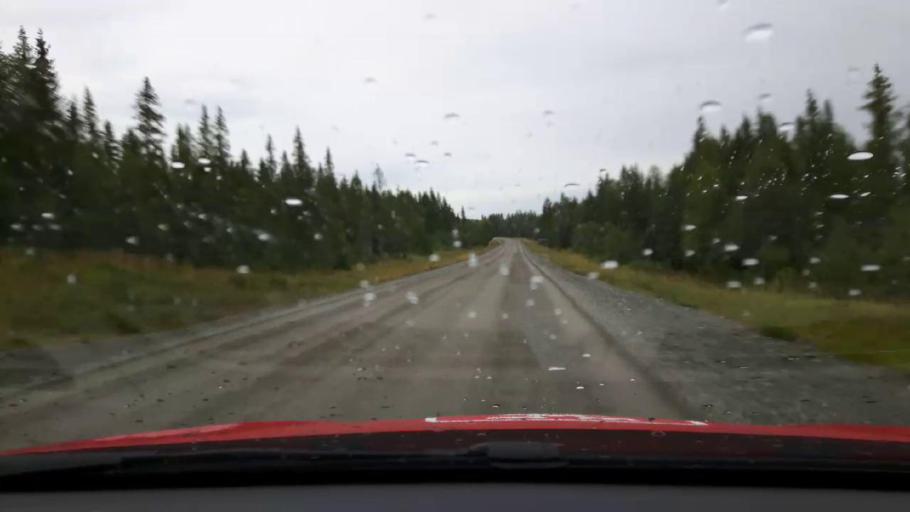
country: SE
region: Jaemtland
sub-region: Are Kommun
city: Are
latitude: 63.4663
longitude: 12.6163
